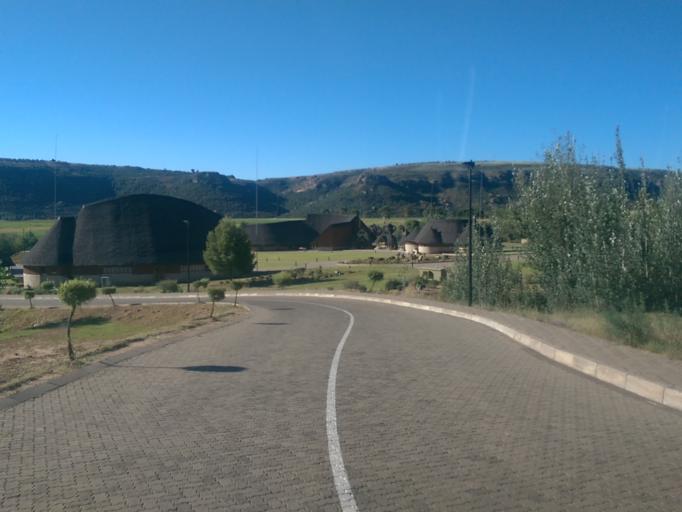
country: LS
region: Maseru
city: Maseru
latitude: -29.3472
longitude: 27.6627
